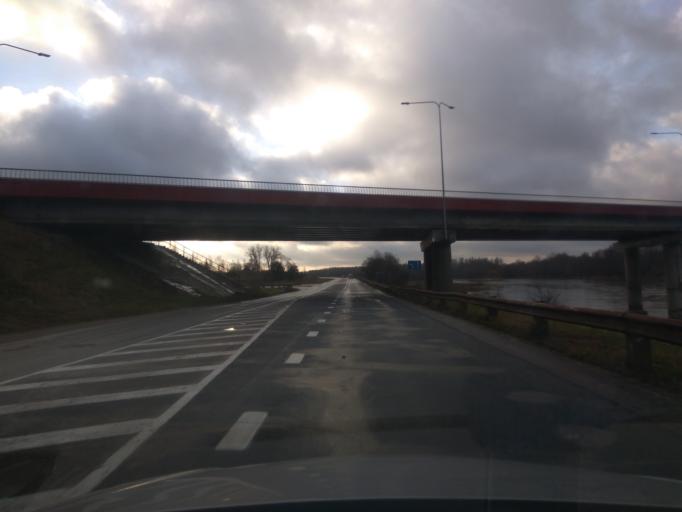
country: LV
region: Kuldigas Rajons
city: Kuldiga
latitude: 56.9625
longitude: 22.0034
